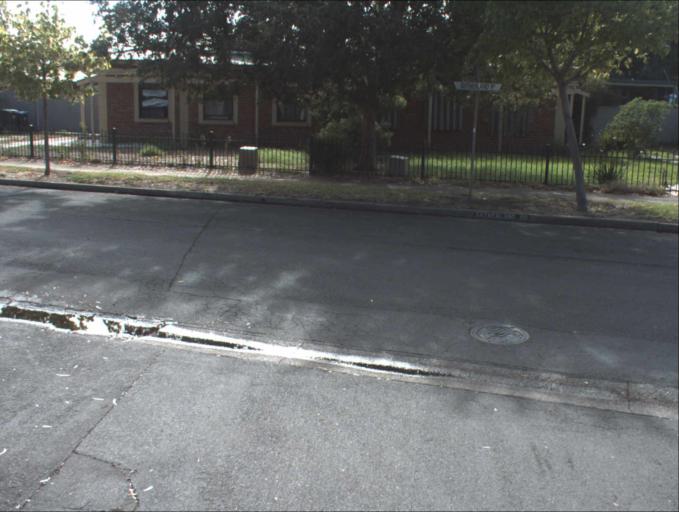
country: AU
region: South Australia
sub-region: Charles Sturt
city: Woodville North
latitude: -34.8649
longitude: 138.5621
